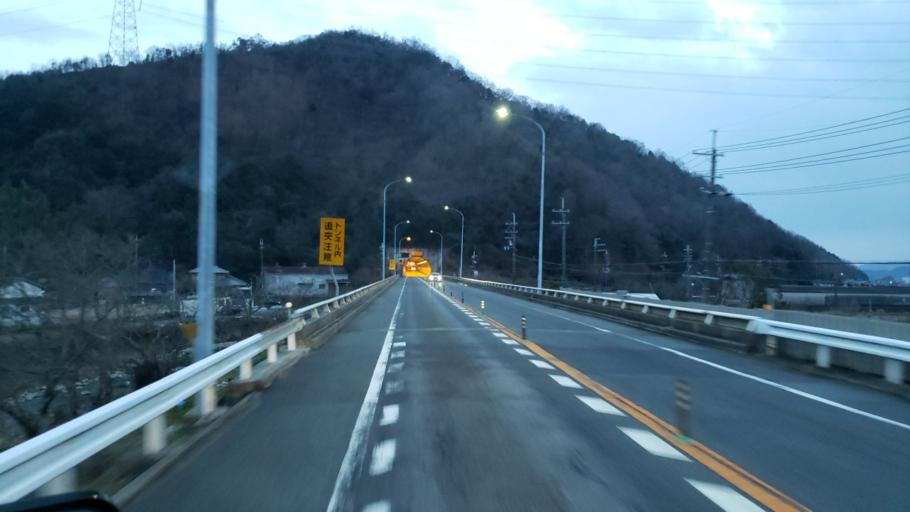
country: JP
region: Hyogo
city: Himeji
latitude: 34.9726
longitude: 134.7689
